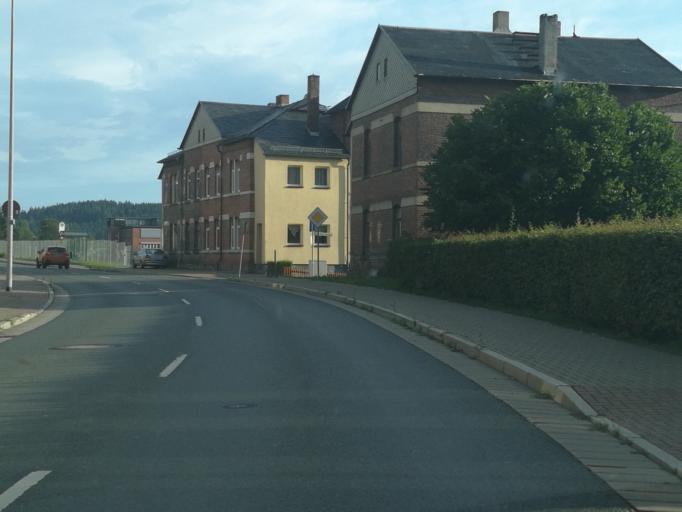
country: DE
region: Saxony
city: Adorf
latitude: 50.3253
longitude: 12.2573
